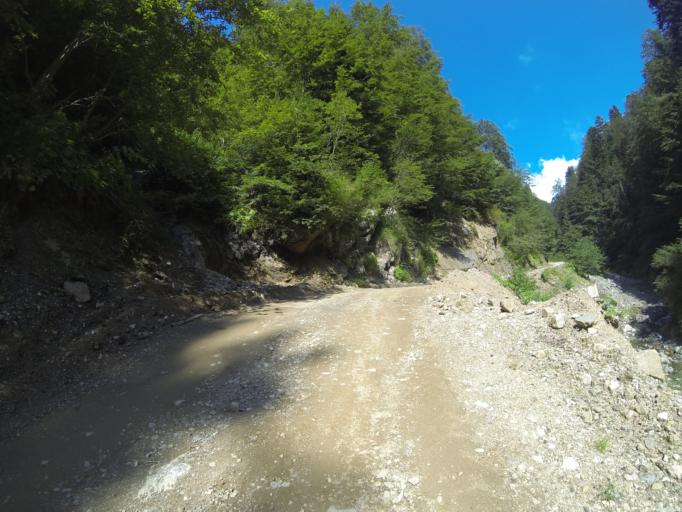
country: RO
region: Valcea
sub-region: Comuna Costesti
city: Bistrita
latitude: 45.2580
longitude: 23.9890
